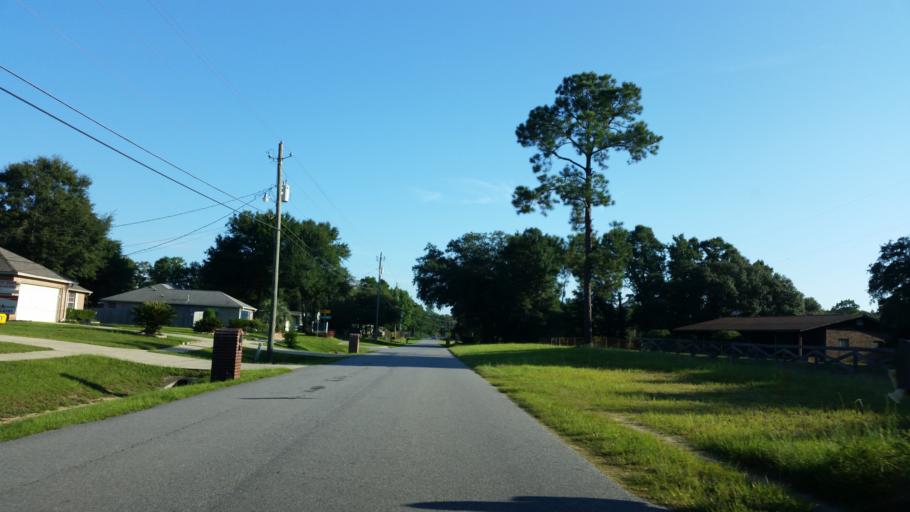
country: US
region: Florida
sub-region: Escambia County
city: Bellview
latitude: 30.5018
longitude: -87.3566
